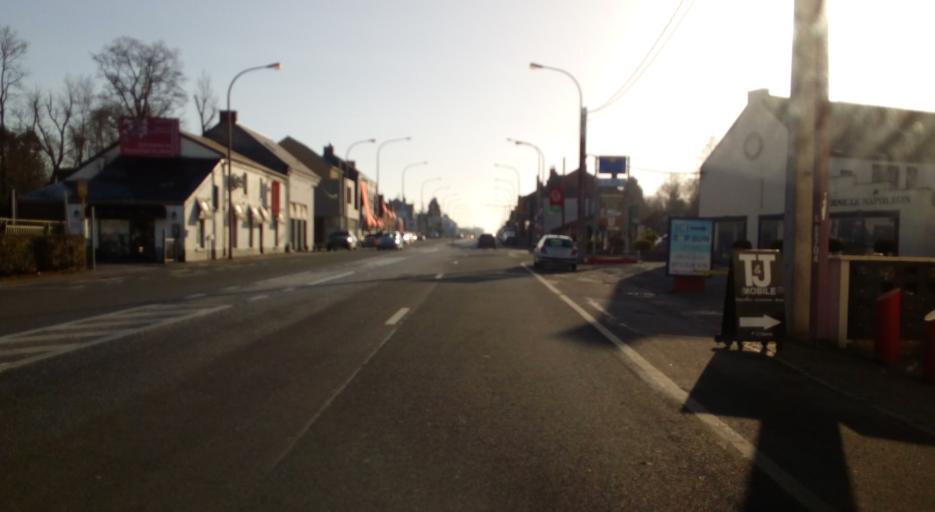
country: BE
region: Wallonia
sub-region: Province du Hainaut
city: Gerpinnes
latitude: 50.3429
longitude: 4.4733
